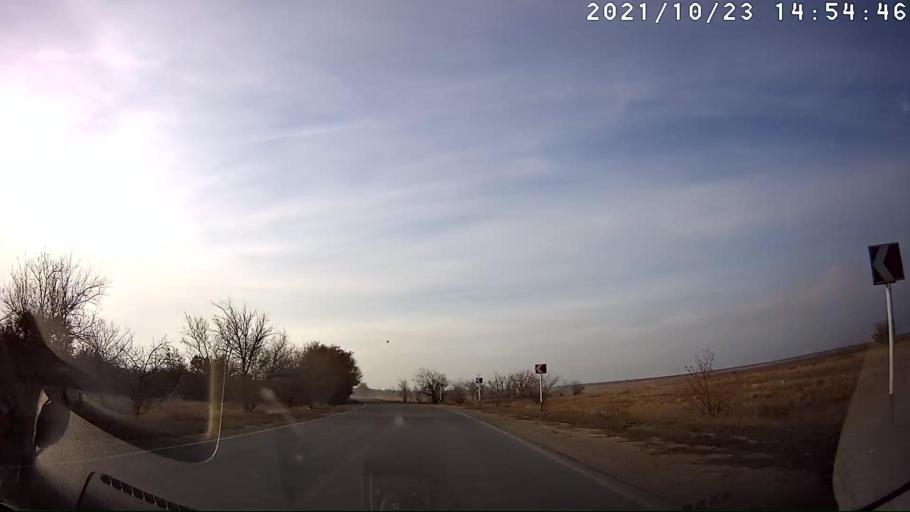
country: RU
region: Volgograd
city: Volgograd
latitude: 48.4510
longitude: 44.4104
